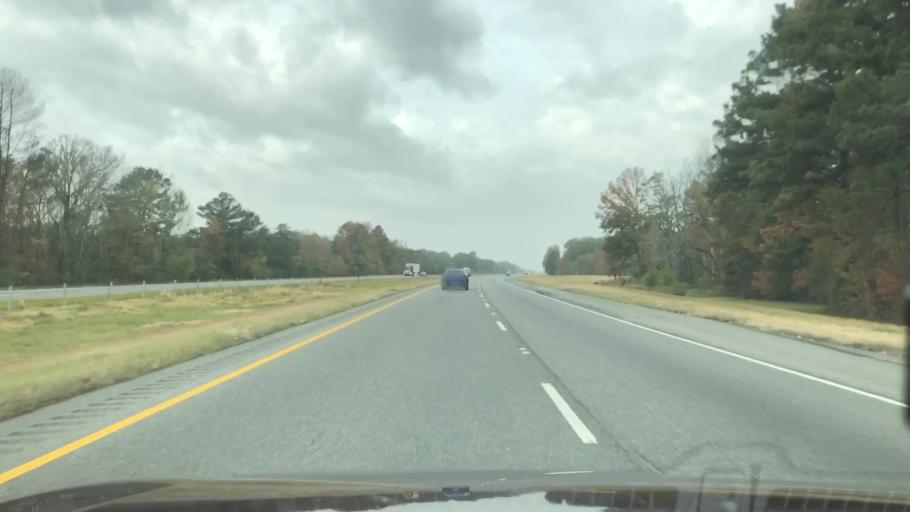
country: US
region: Louisiana
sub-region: Richland Parish
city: Delhi
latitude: 32.4459
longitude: -91.5429
